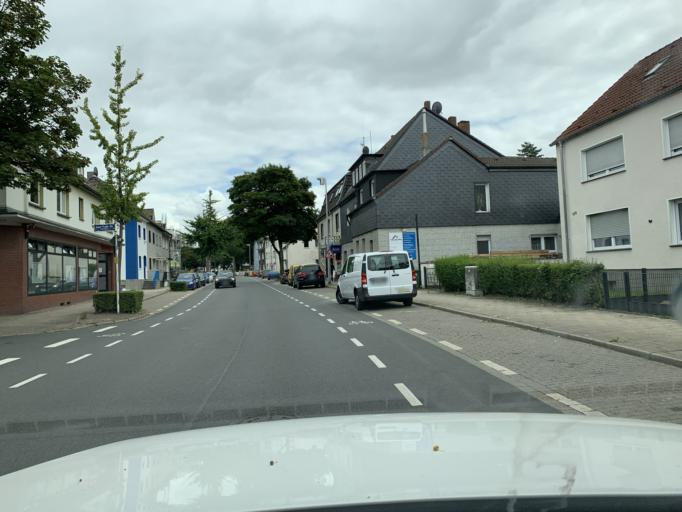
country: DE
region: North Rhine-Westphalia
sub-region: Regierungsbezirk Dusseldorf
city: Oberhausen
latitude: 51.4565
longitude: 6.9046
